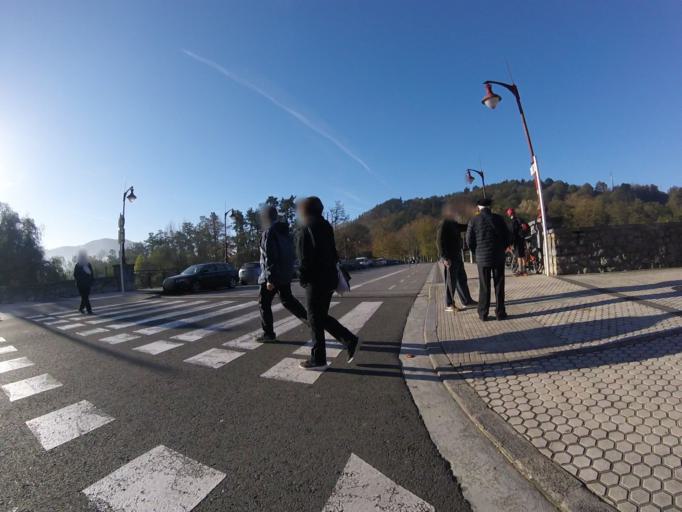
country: ES
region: Basque Country
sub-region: Provincia de Guipuzcoa
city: Lasarte
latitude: 43.2683
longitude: -2.0228
